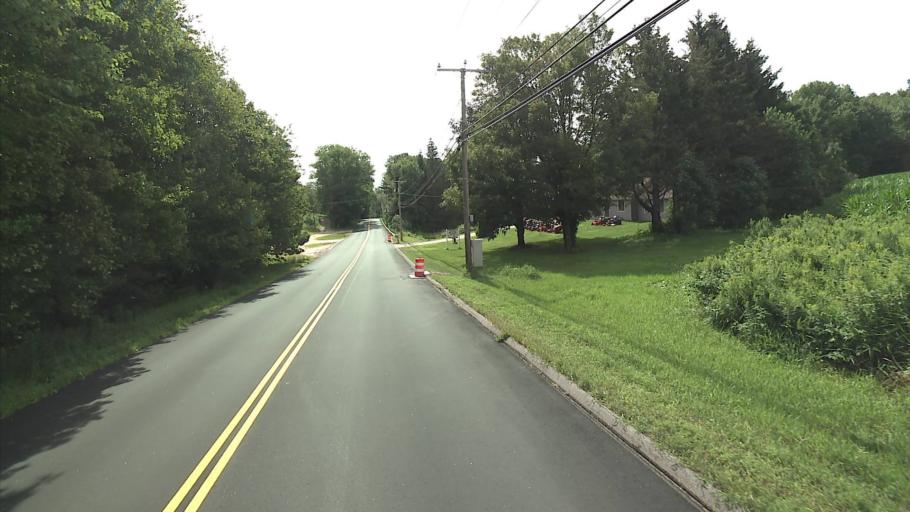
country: US
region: Connecticut
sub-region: Windham County
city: South Woodstock
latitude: 41.9505
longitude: -72.0281
